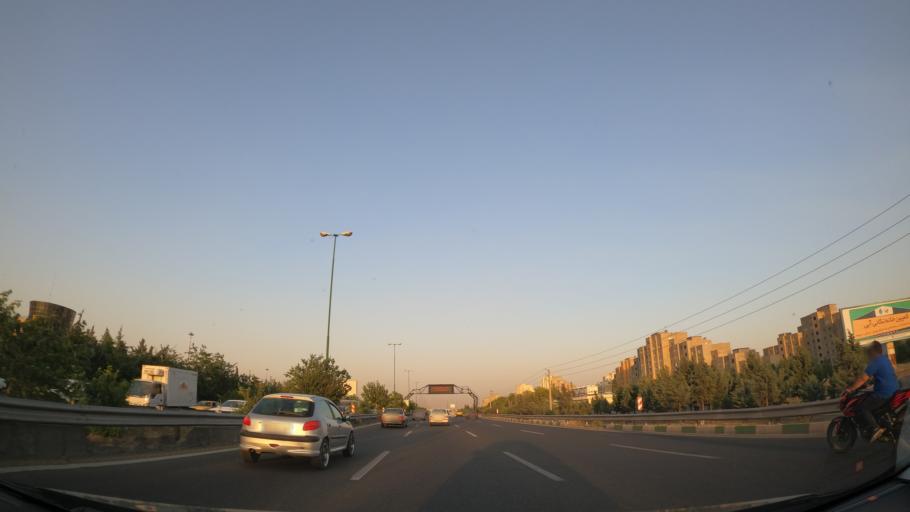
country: IR
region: Tehran
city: Tehran
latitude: 35.7154
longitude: 51.3204
